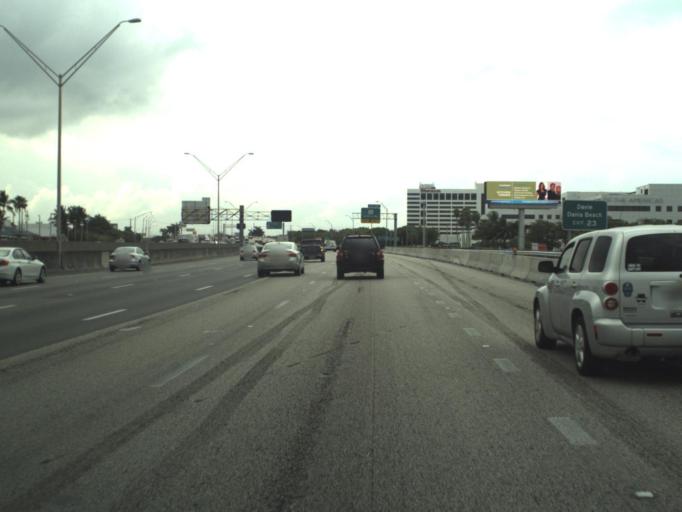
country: US
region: Florida
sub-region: Broward County
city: Dania Beach
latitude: 26.0559
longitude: -80.1622
